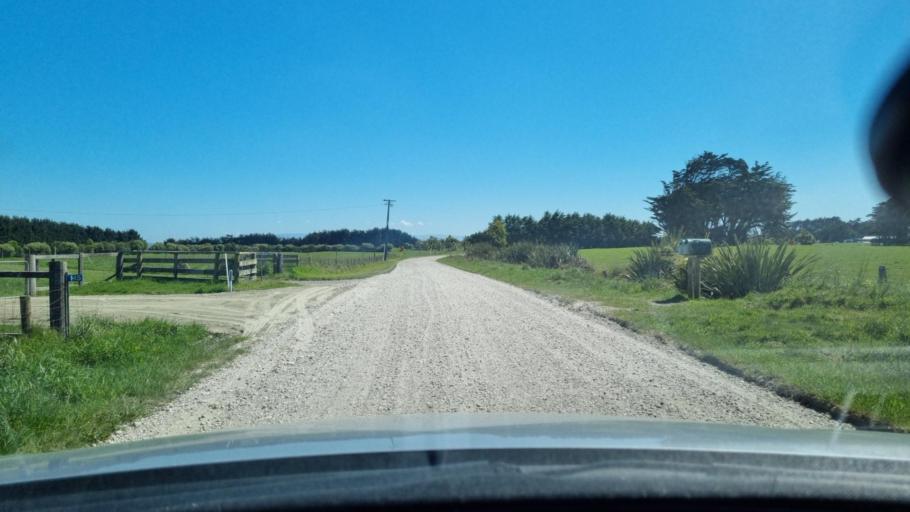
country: NZ
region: Southland
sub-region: Invercargill City
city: Invercargill
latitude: -46.4160
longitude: 168.2649
